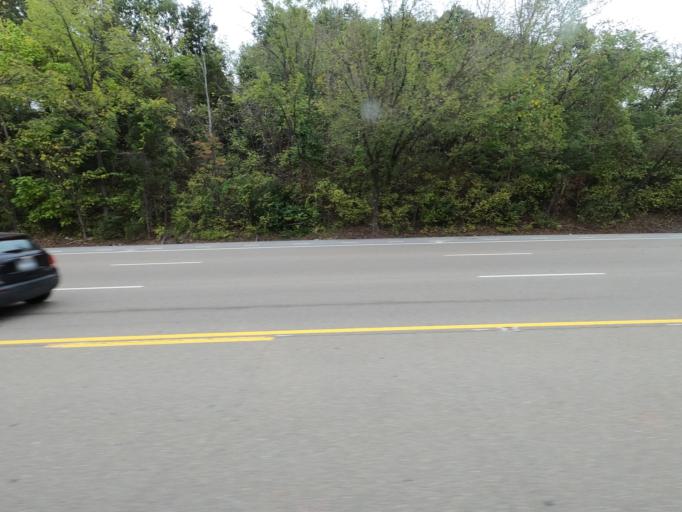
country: US
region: Tennessee
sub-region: Sullivan County
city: Kingsport
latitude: 36.5589
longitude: -82.5469
